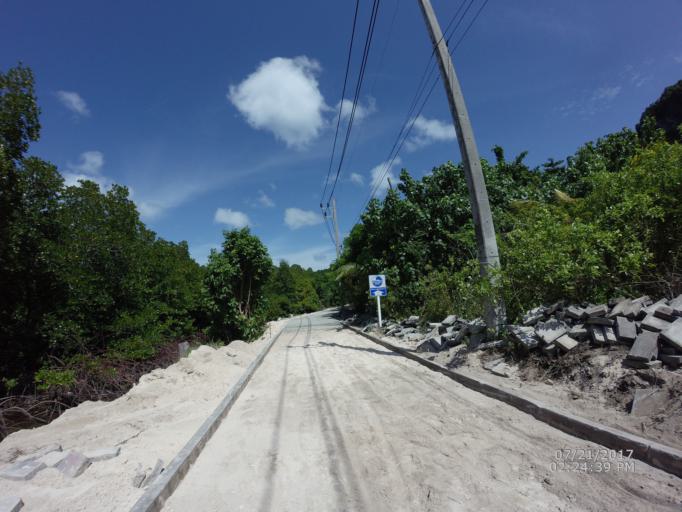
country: TH
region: Phangnga
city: Ban Phru Nai
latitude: 7.7602
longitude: 98.7670
